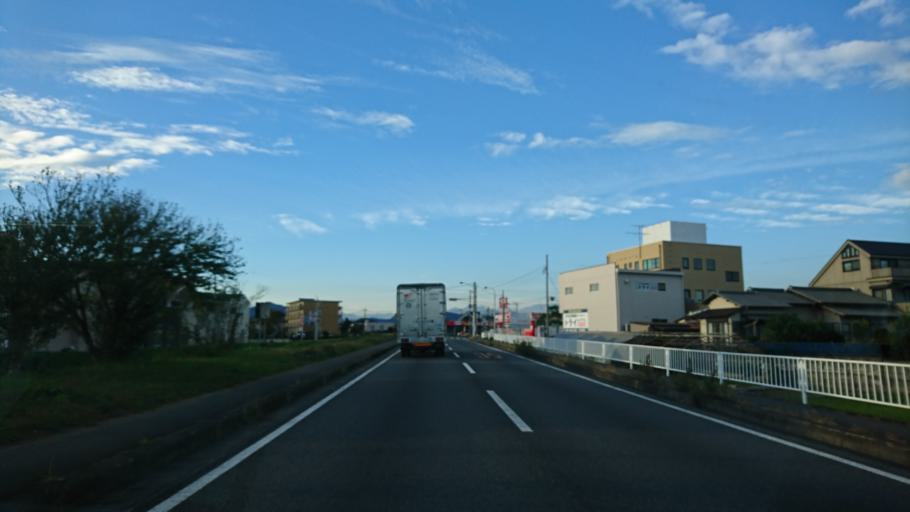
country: JP
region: Shizuoka
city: Fuji
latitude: 35.1436
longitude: 138.6474
